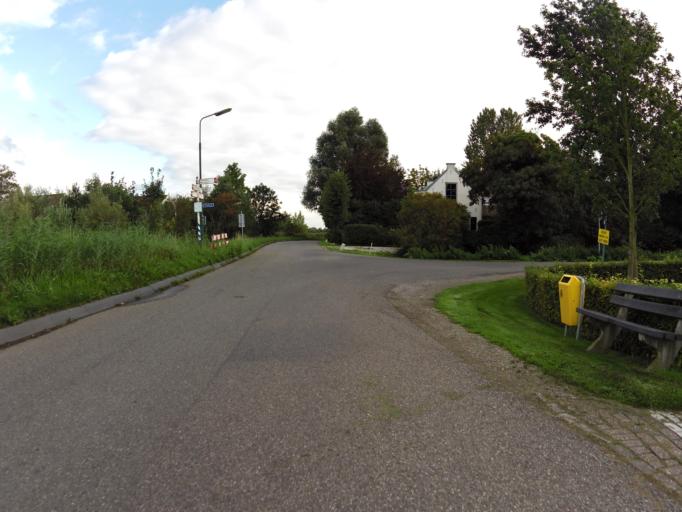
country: NL
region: Utrecht
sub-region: Stichtse Vecht
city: Breukelen
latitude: 52.1442
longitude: 4.9517
